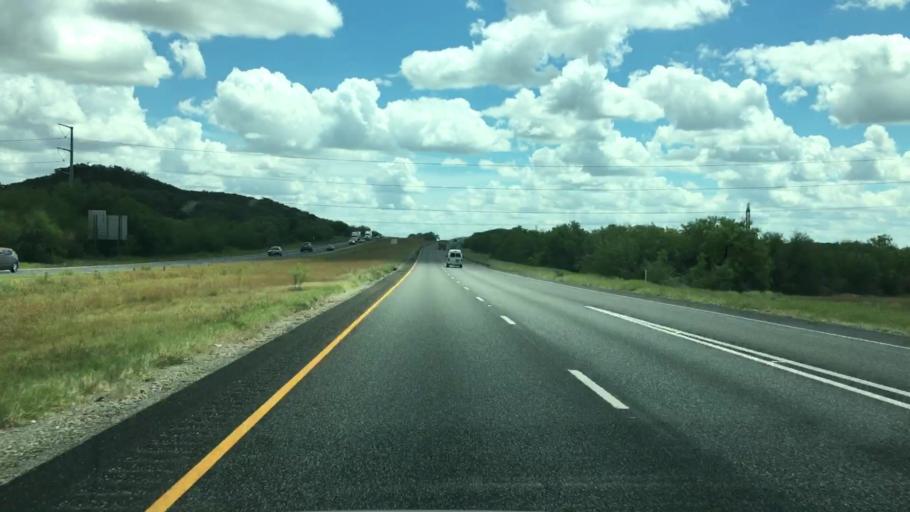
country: US
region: Texas
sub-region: Live Oak County
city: Three Rivers
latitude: 28.7268
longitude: -98.2873
